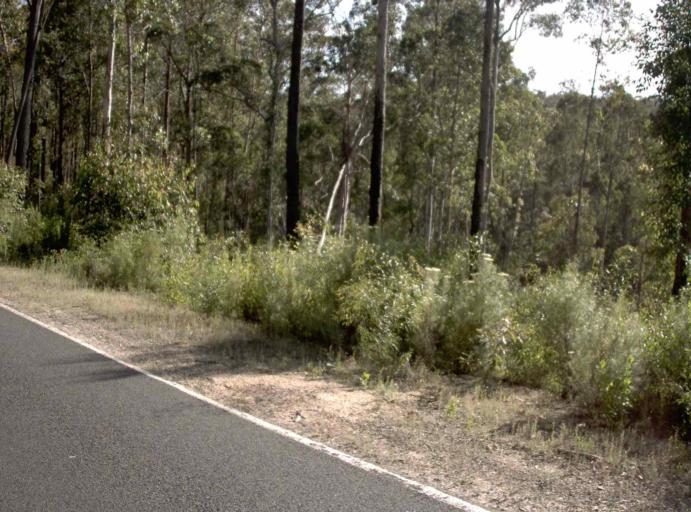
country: AU
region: Victoria
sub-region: East Gippsland
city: Lakes Entrance
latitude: -37.6667
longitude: 148.4780
